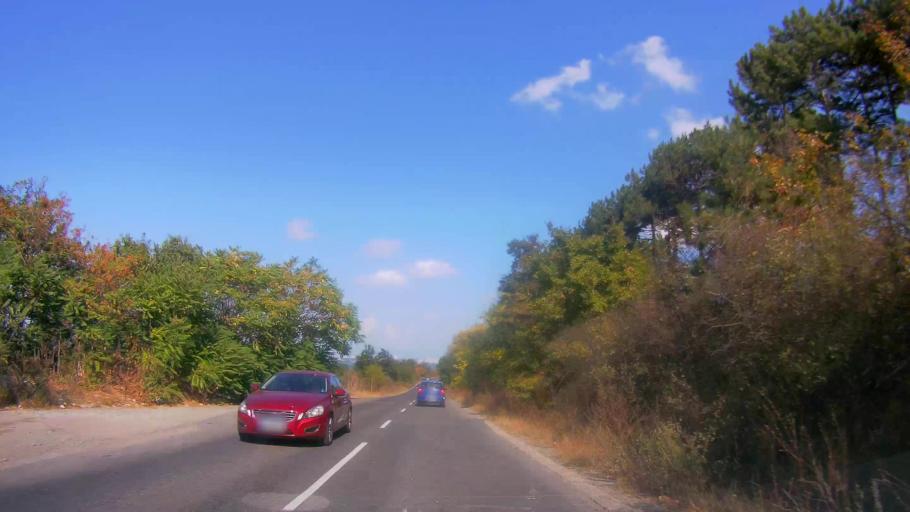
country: BG
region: Burgas
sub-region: Obshtina Burgas
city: Burgas
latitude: 42.4752
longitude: 27.4005
